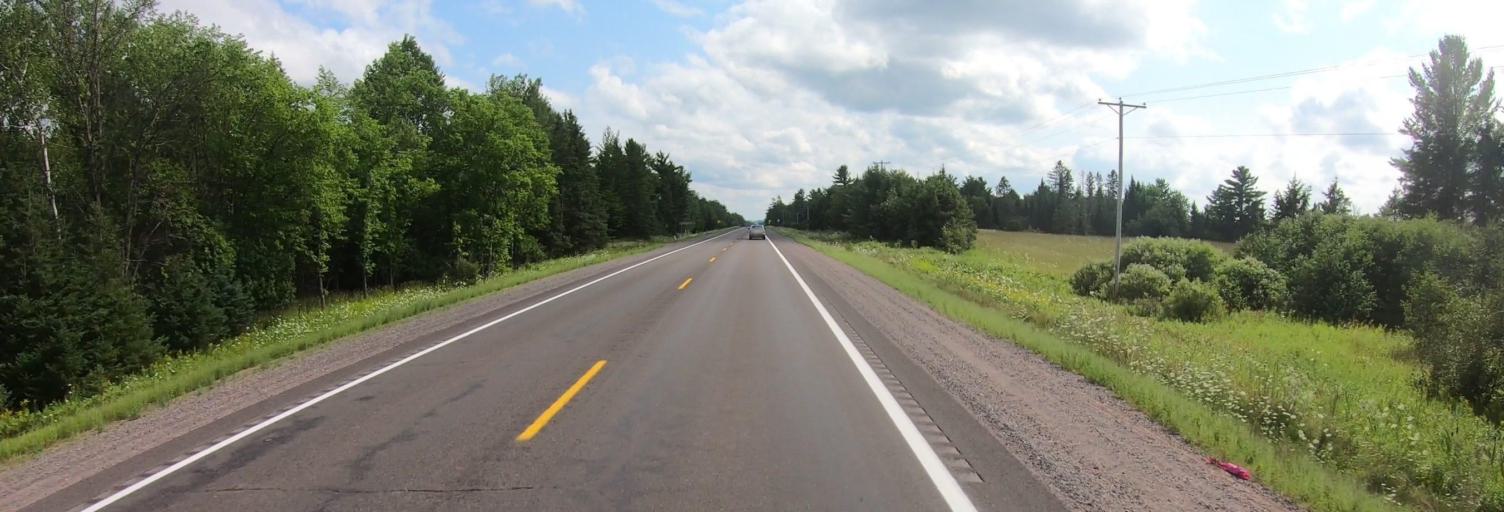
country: US
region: Michigan
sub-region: Ontonagon County
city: Ontonagon
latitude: 46.5630
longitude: -89.1785
